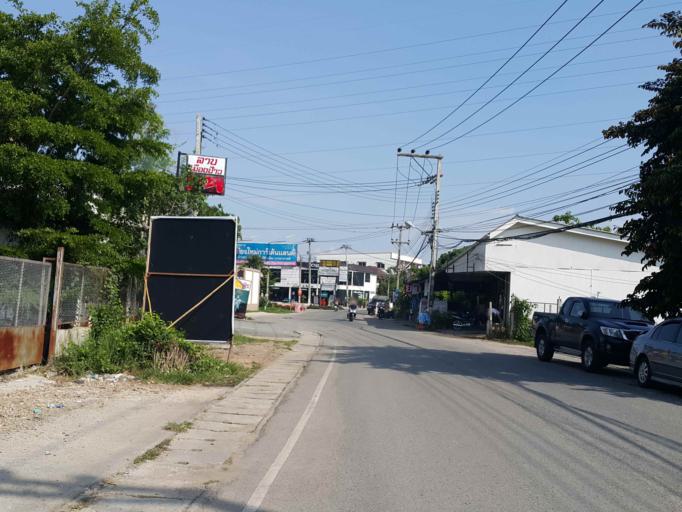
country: TH
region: Chiang Mai
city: San Sai
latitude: 18.8200
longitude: 99.0197
